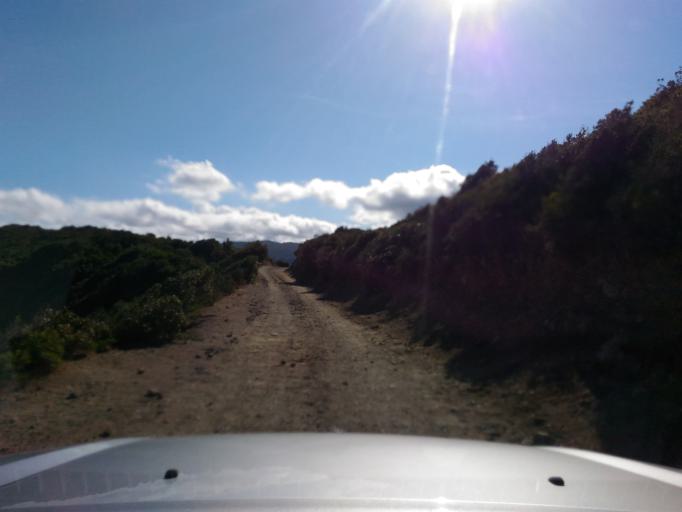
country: FR
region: Corsica
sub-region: Departement de la Haute-Corse
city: Brando
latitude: 42.9716
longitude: 9.4547
